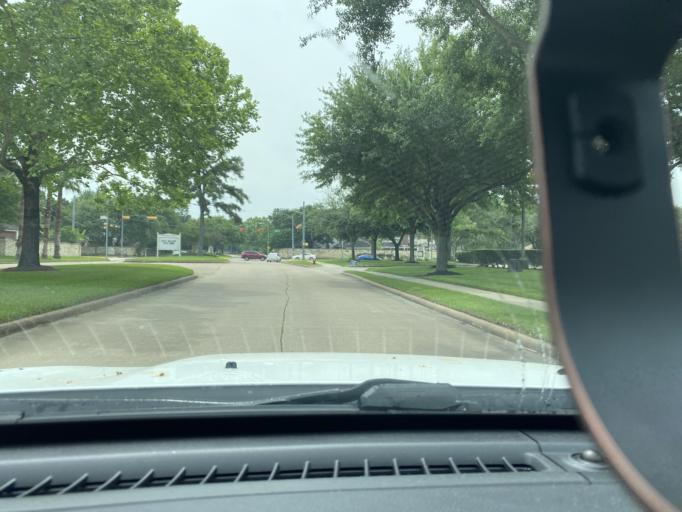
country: US
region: Texas
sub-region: Harris County
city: Jersey Village
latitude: 29.9097
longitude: -95.5736
